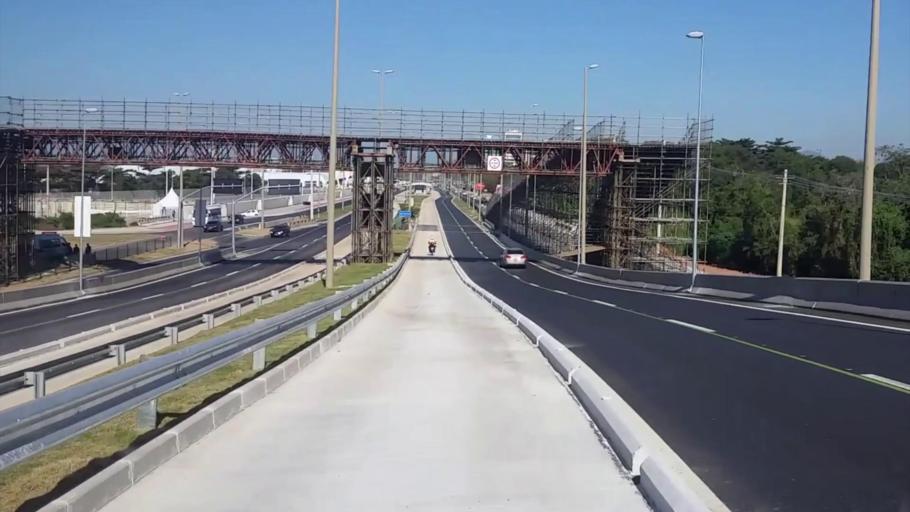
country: BR
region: Rio de Janeiro
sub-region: Nilopolis
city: Nilopolis
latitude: -22.9670
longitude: -43.3974
